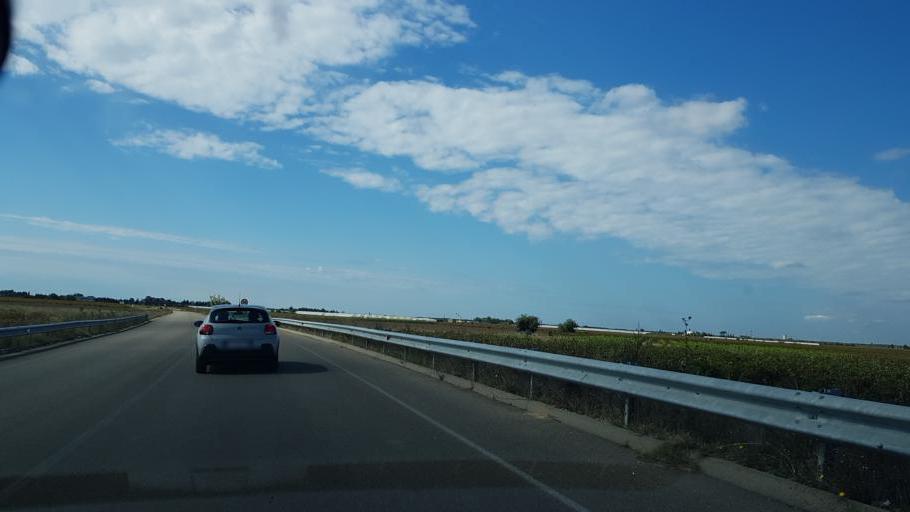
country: IT
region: Apulia
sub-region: Provincia di Lecce
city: Leverano
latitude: 40.3009
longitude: 17.9784
